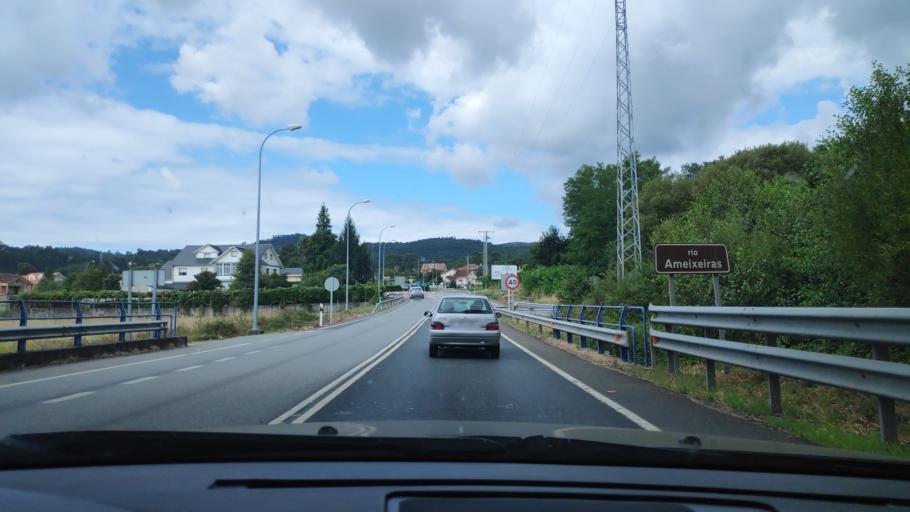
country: ES
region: Galicia
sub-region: Provincia de Pontevedra
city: Portas
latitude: 42.5955
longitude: -8.6851
